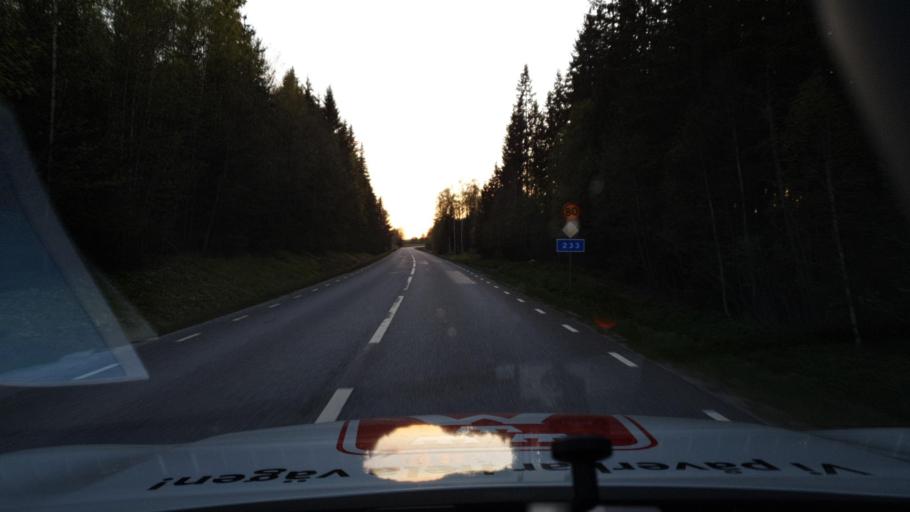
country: SE
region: Vaestmanland
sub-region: Skinnskattebergs Kommun
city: Skinnskatteberg
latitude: 59.8851
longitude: 15.6264
